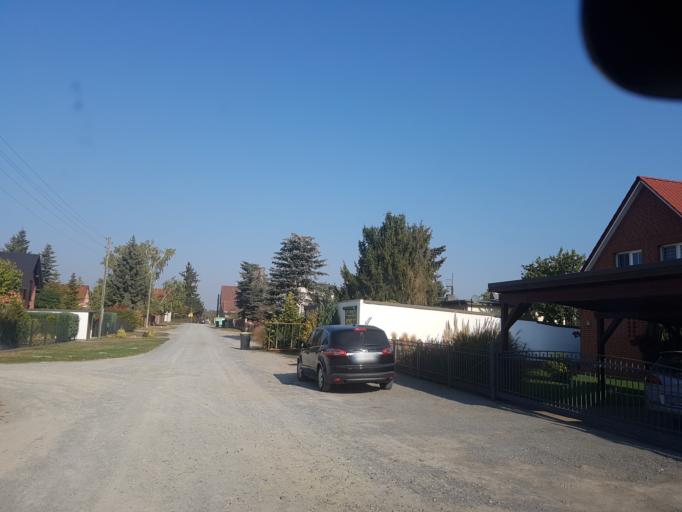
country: DE
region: Brandenburg
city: Finsterwalde
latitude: 51.6160
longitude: 13.7180
